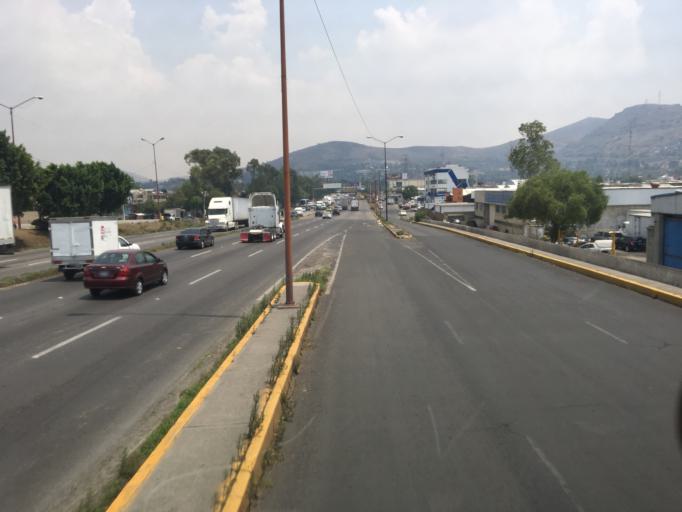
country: MX
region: Mexico
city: Tlalnepantla
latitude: 19.5475
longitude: -99.1833
